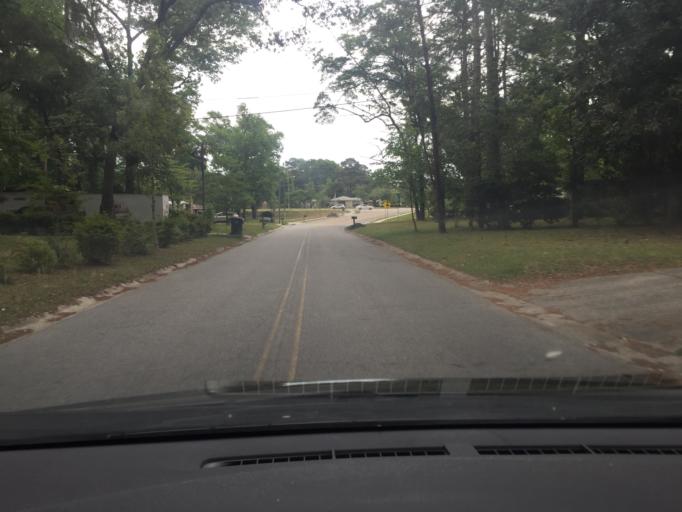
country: US
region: Georgia
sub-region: Chatham County
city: Montgomery
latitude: 31.9814
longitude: -81.1075
